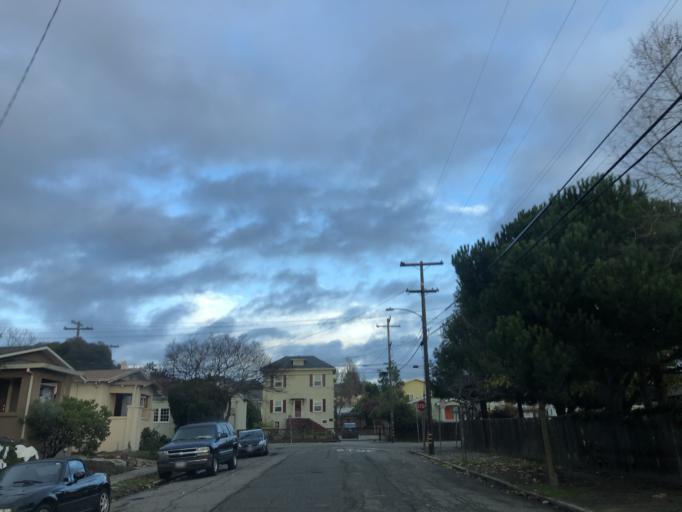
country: US
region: California
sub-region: Alameda County
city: Berkeley
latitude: 37.8474
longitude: -122.2629
